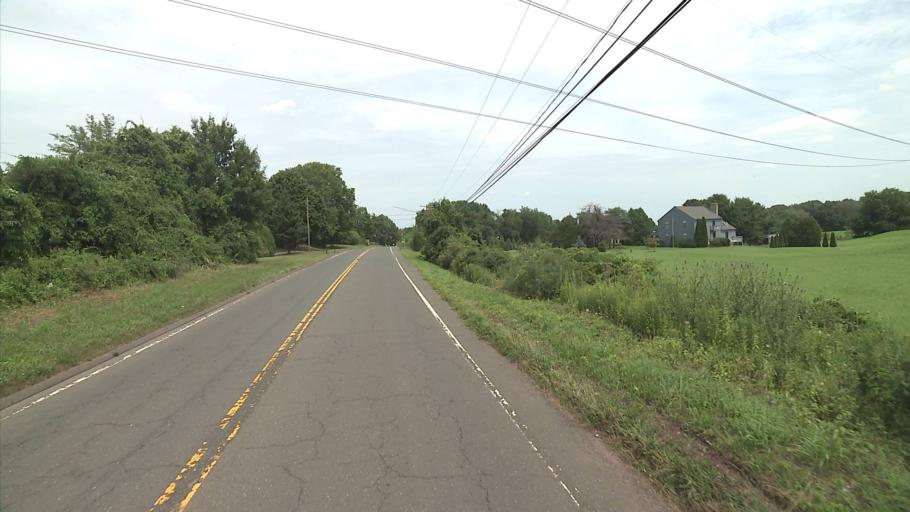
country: US
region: Connecticut
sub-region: New Haven County
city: Meriden
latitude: 41.5828
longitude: -72.8046
